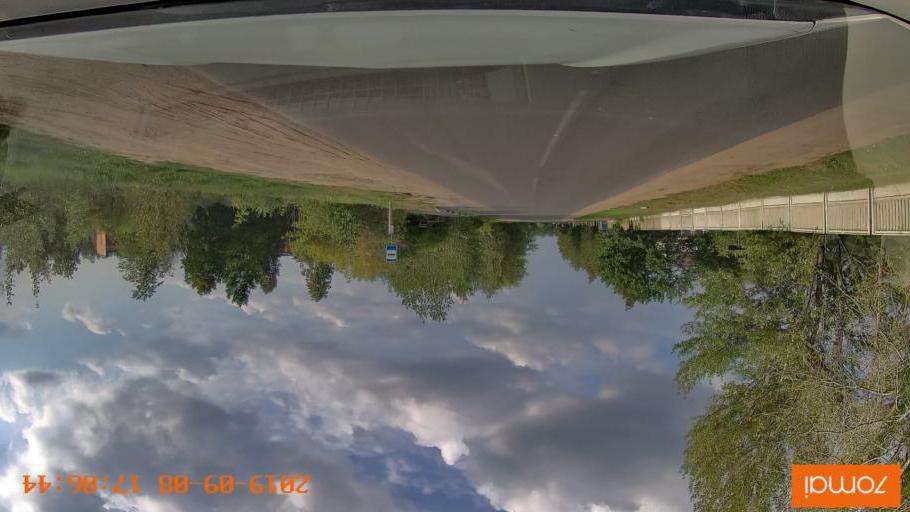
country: BY
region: Grodnenskaya
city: Hrodna
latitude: 53.6681
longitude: 23.9522
